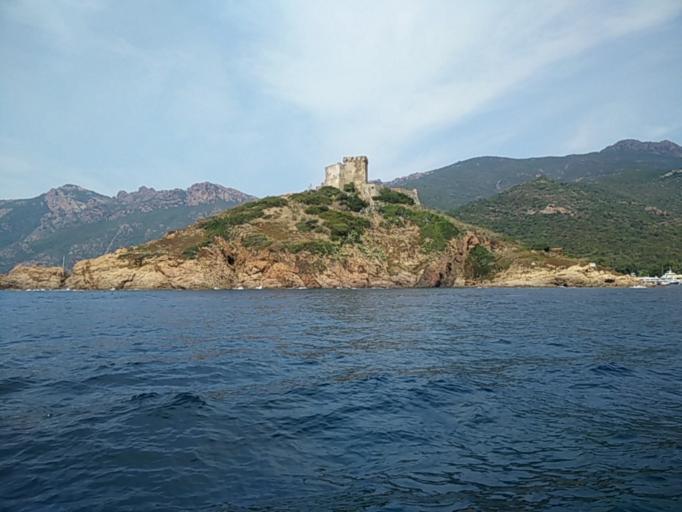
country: FR
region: Corsica
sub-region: Departement de la Corse-du-Sud
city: Cargese
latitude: 42.3460
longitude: 8.6145
